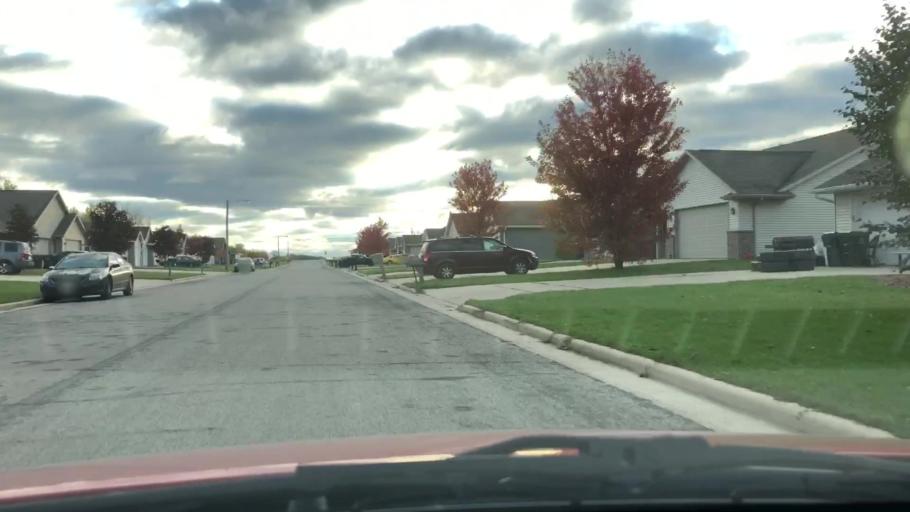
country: US
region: Wisconsin
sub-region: Outagamie County
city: Seymour
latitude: 44.5098
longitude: -88.3142
